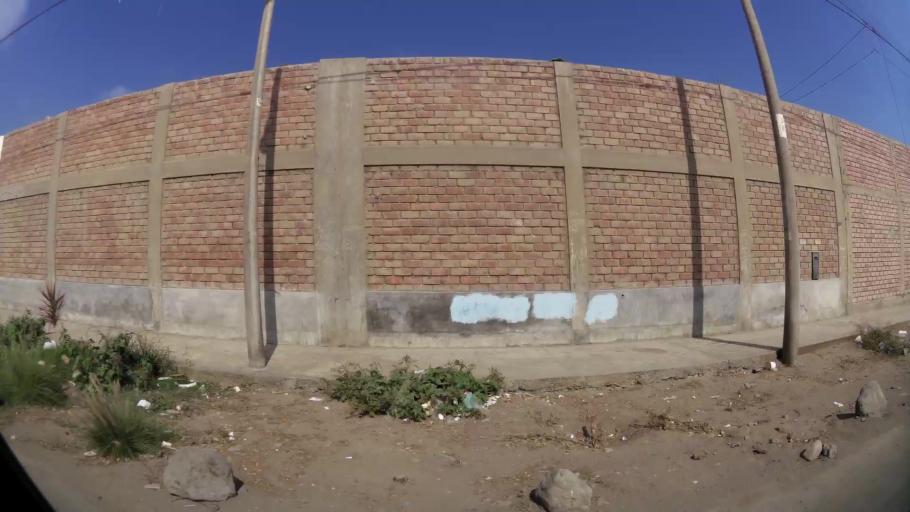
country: PE
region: La Libertad
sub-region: Provincia de Trujillo
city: Trujillo
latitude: -8.1259
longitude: -79.0209
